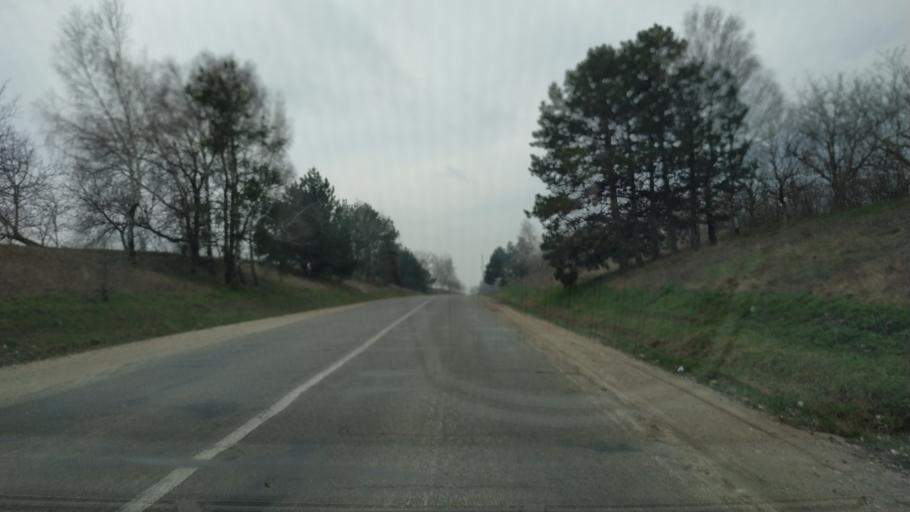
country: MD
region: Cahul
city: Cahul
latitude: 45.9376
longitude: 28.2868
